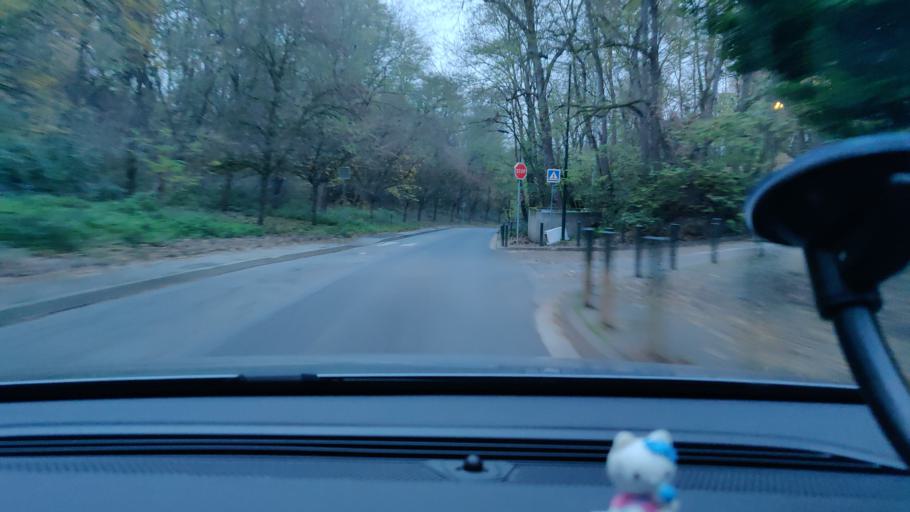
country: FR
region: Midi-Pyrenees
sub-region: Departement de la Haute-Garonne
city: Vieille-Toulouse
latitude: 43.5486
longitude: 1.4487
